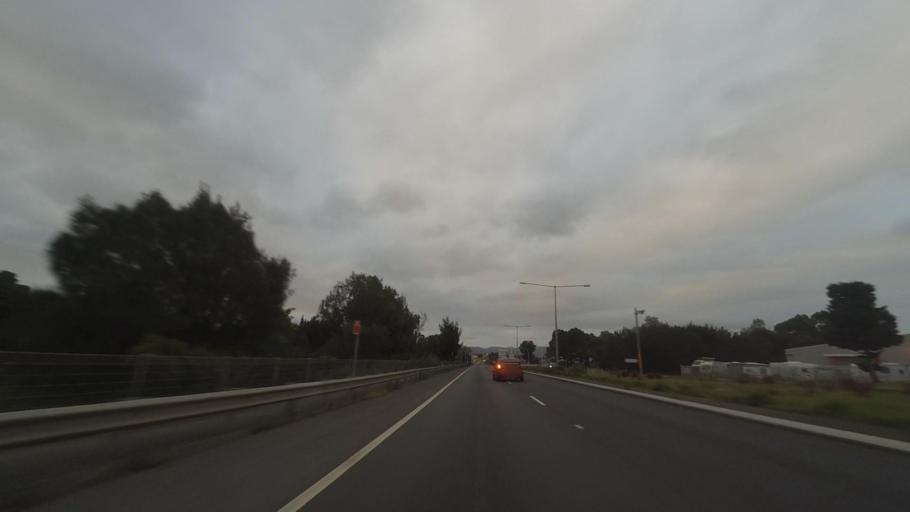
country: AU
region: New South Wales
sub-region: Shellharbour
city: Albion Park Rail
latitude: -34.5483
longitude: 150.7850
